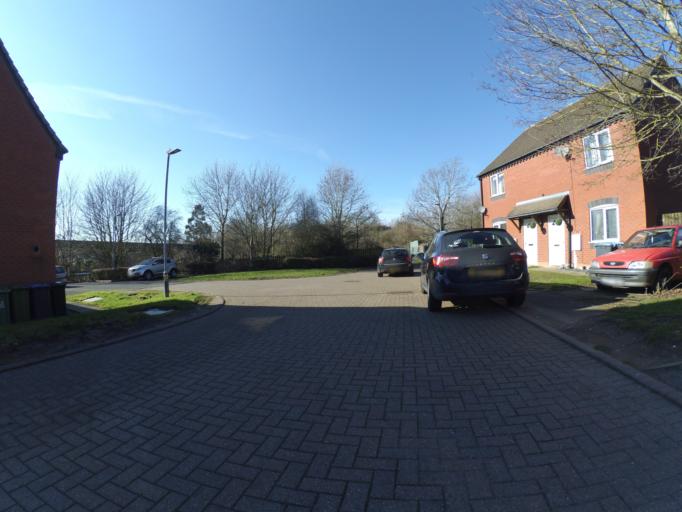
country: GB
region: England
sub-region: Warwickshire
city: Rugby
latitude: 52.3942
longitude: -1.2473
